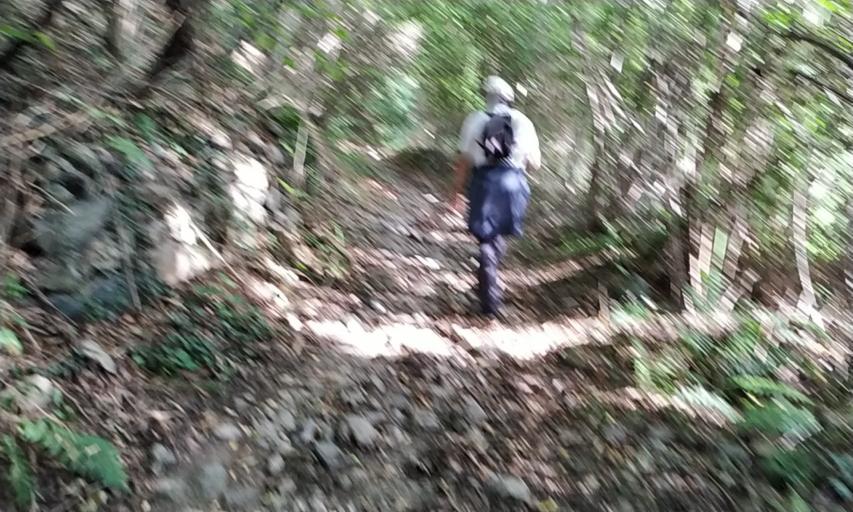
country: IT
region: Piedmont
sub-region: Provincia di Biella
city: Dorzano
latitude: 45.4318
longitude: 8.0853
